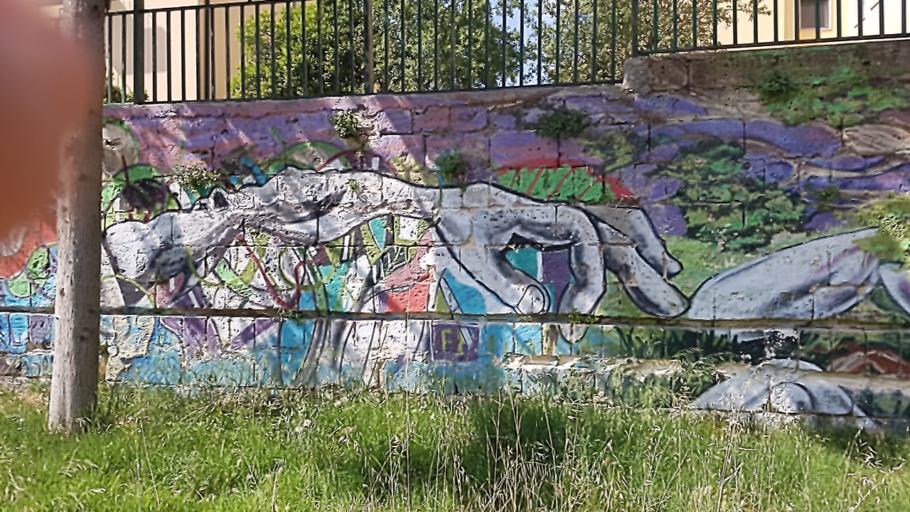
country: IT
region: Apulia
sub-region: Provincia di Bari
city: Gravina in Puglia
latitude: 40.8232
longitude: 16.4131
